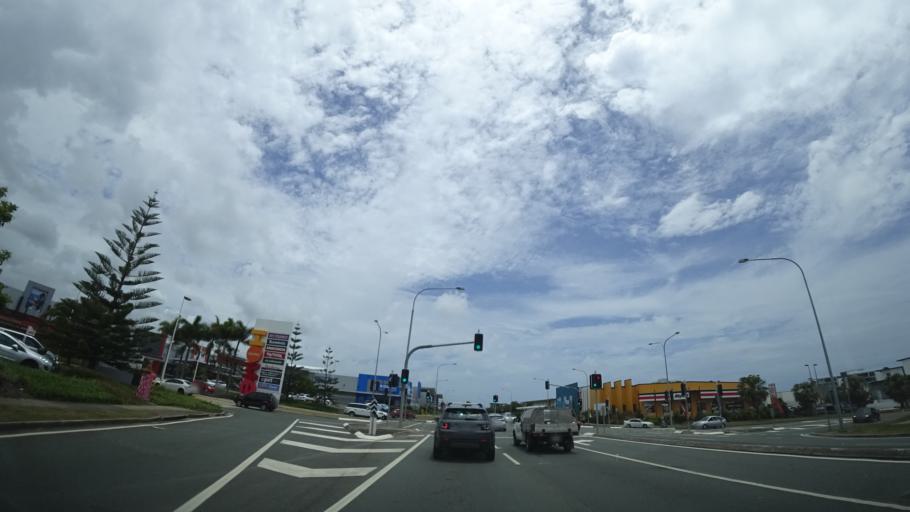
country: AU
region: Queensland
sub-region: Sunshine Coast
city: Dicky Beach
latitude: -26.7365
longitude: 153.1204
